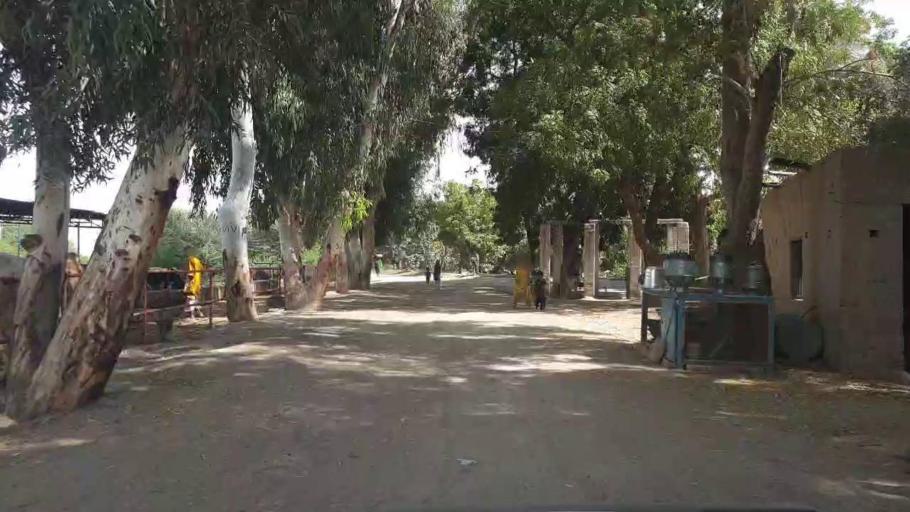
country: PK
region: Sindh
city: Kunri
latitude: 25.2168
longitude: 69.6880
